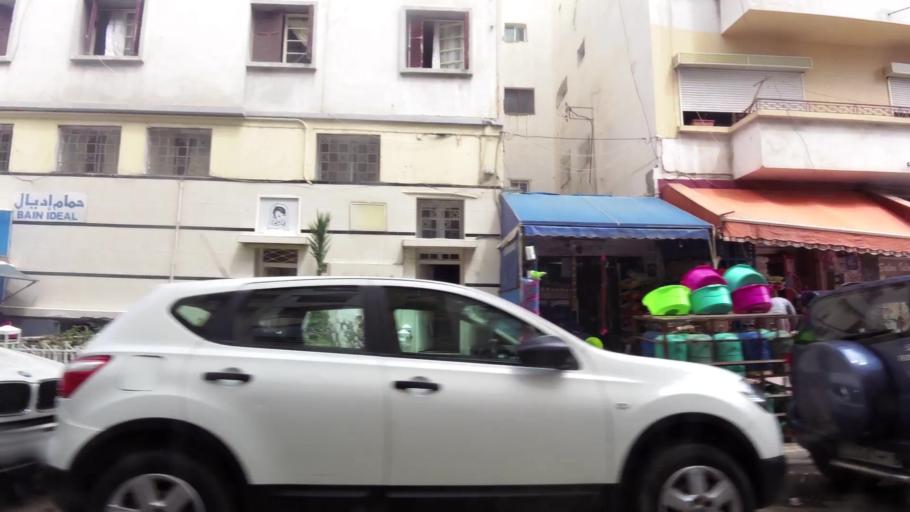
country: MA
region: Grand Casablanca
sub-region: Casablanca
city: Casablanca
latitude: 33.5953
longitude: -7.6401
